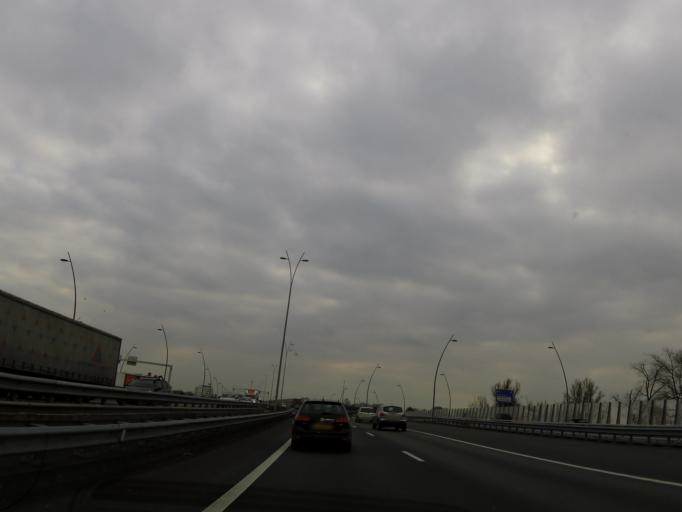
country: NL
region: North Brabant
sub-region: Gemeente Eindhoven
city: Meerhoven
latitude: 51.4369
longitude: 5.4259
